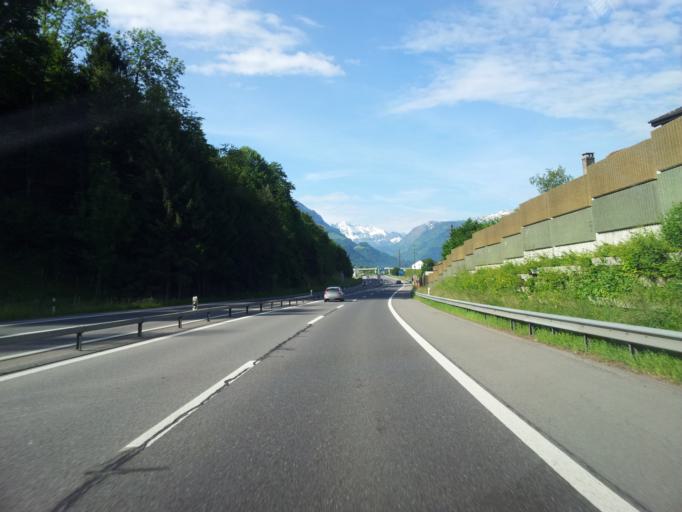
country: CH
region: Obwalden
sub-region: Obwalden
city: Sarnen
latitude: 46.8933
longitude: 8.2560
